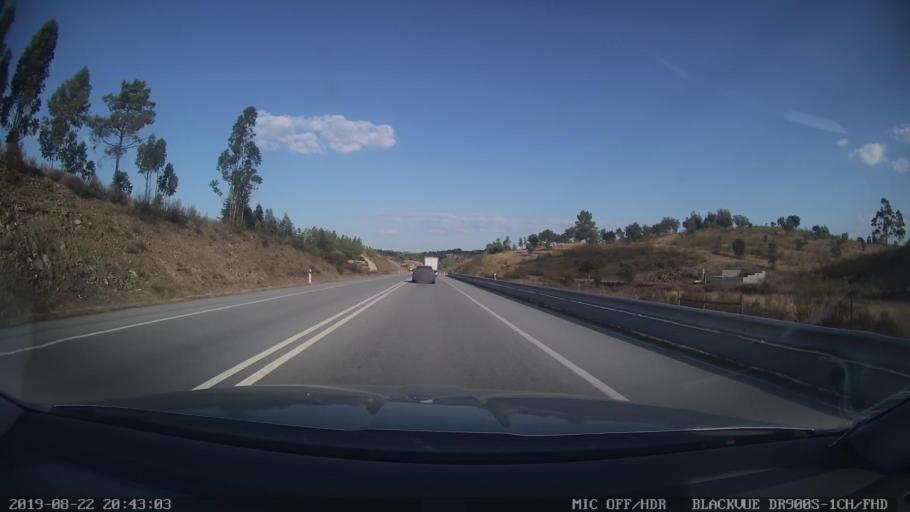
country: PT
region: Castelo Branco
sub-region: Proenca-A-Nova
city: Proenca-a-Nova
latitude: 39.6983
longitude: -7.8255
